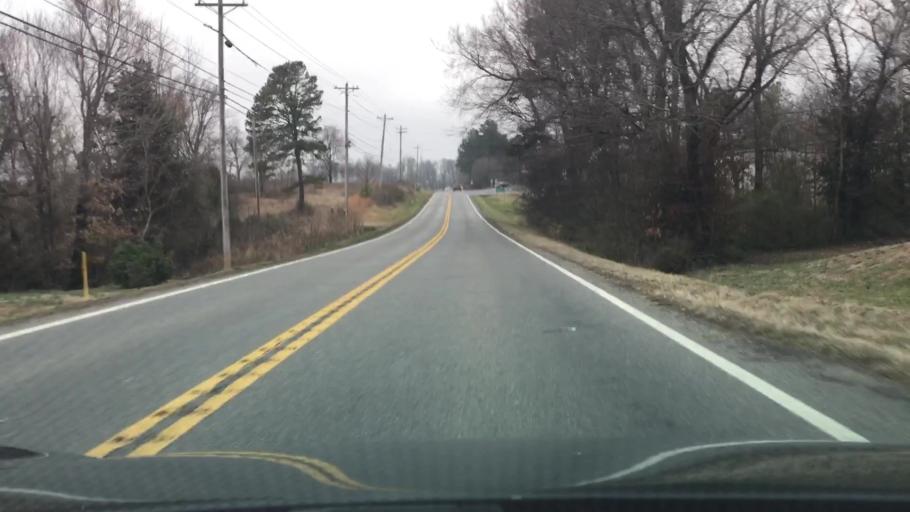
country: US
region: Kentucky
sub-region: Marshall County
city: Benton
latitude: 36.9453
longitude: -88.3644
